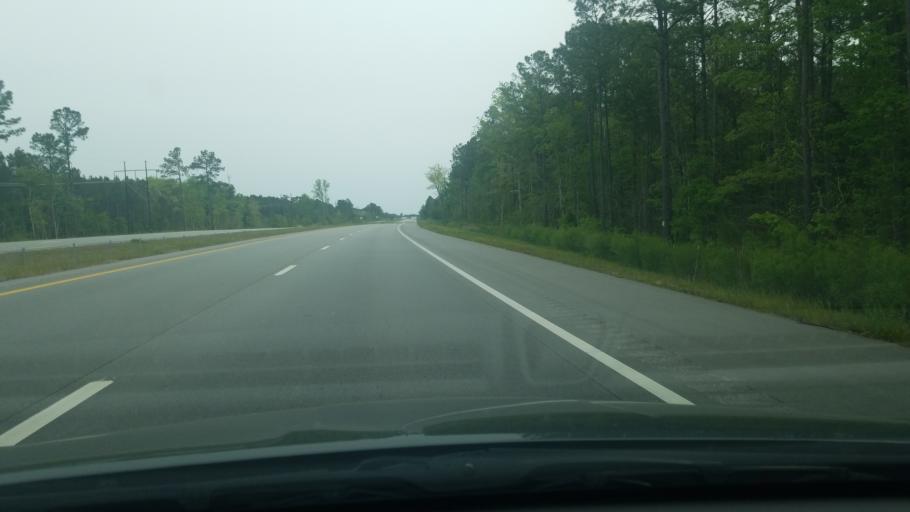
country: US
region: North Carolina
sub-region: Craven County
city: River Bend
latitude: 35.0375
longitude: -77.2231
